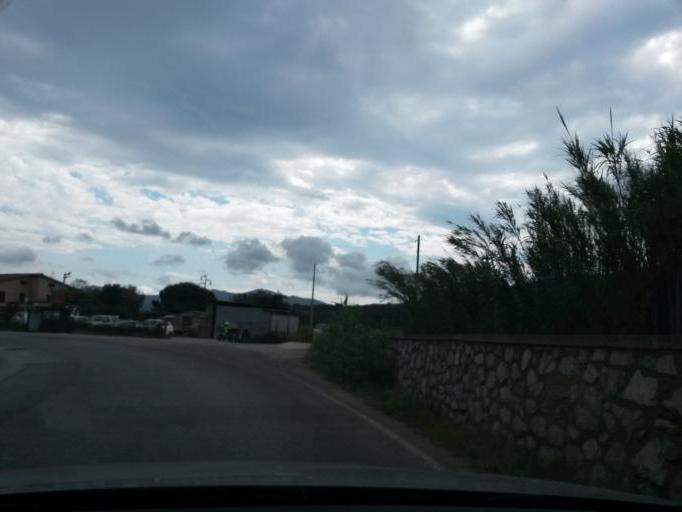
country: IT
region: Tuscany
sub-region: Provincia di Livorno
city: Portoferraio
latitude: 42.7978
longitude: 10.3029
